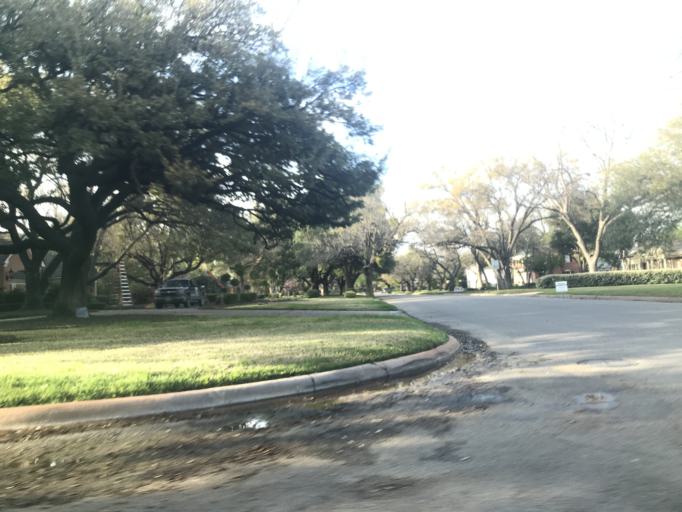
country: US
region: Texas
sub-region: Taylor County
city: Abilene
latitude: 32.4335
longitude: -99.7717
